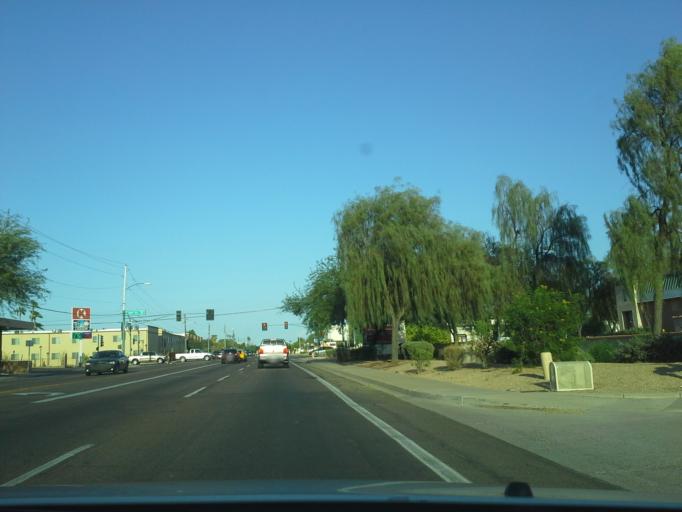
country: US
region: Arizona
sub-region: Maricopa County
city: Guadalupe
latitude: 33.3926
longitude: -111.9970
